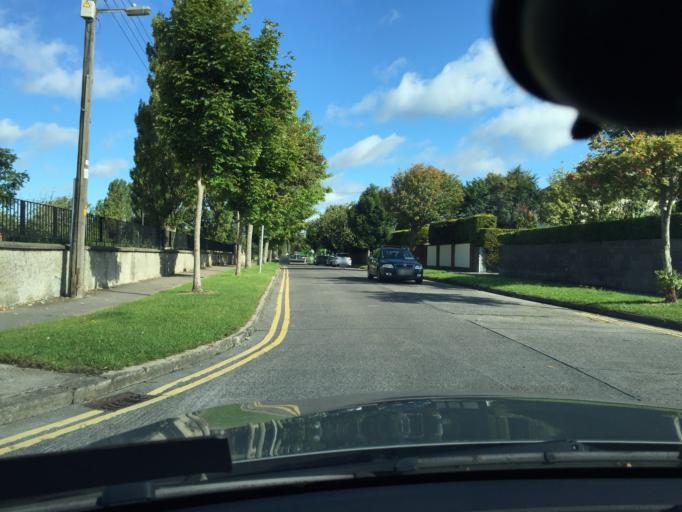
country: IE
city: Palmerstown
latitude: 53.3520
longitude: -6.3675
